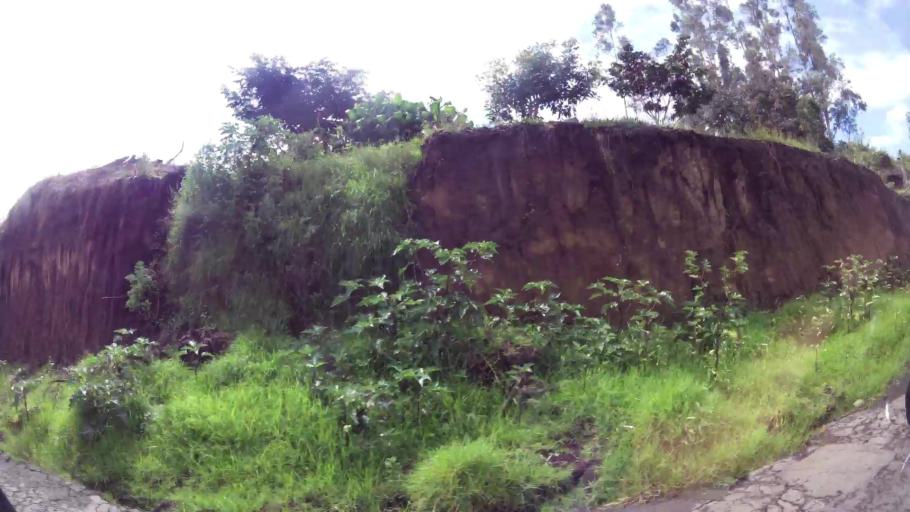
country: EC
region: Pichincha
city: Sangolqui
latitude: -0.3063
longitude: -78.4258
